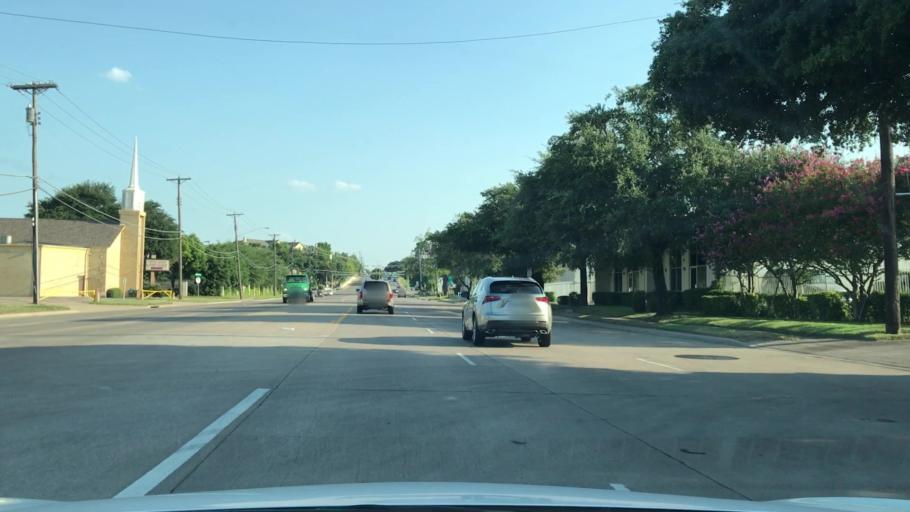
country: US
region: Texas
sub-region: Dallas County
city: Dallas
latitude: 32.7672
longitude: -96.8229
